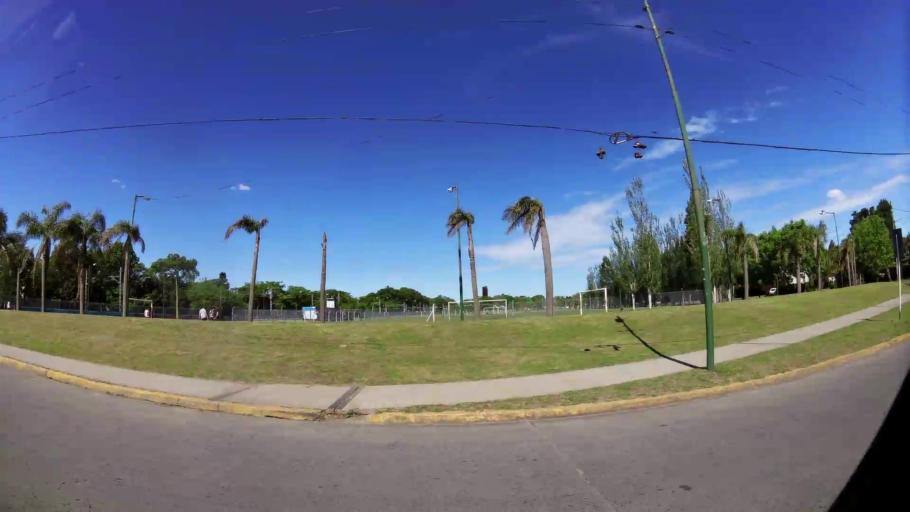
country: AR
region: Buenos Aires
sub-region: Partido de Almirante Brown
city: Adrogue
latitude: -34.7962
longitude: -58.3640
